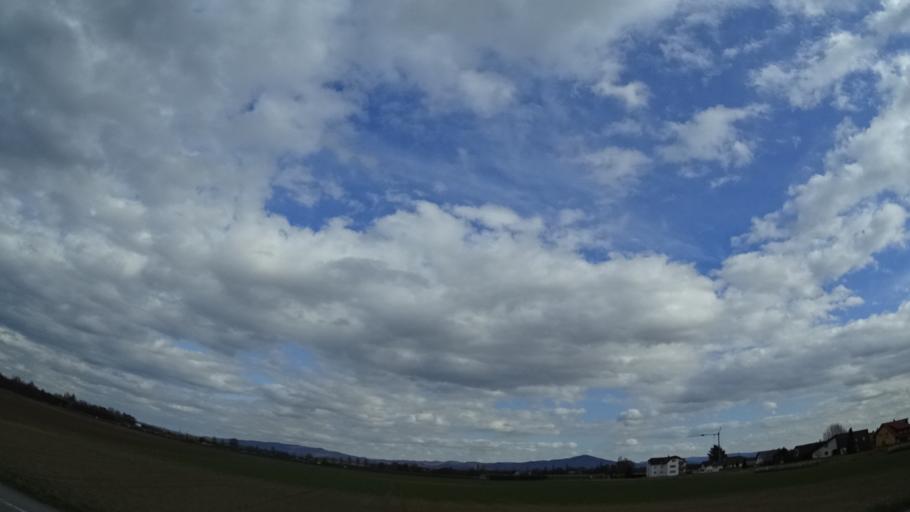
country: DE
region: Hesse
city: Gernsheim
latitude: 49.7385
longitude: 8.4889
